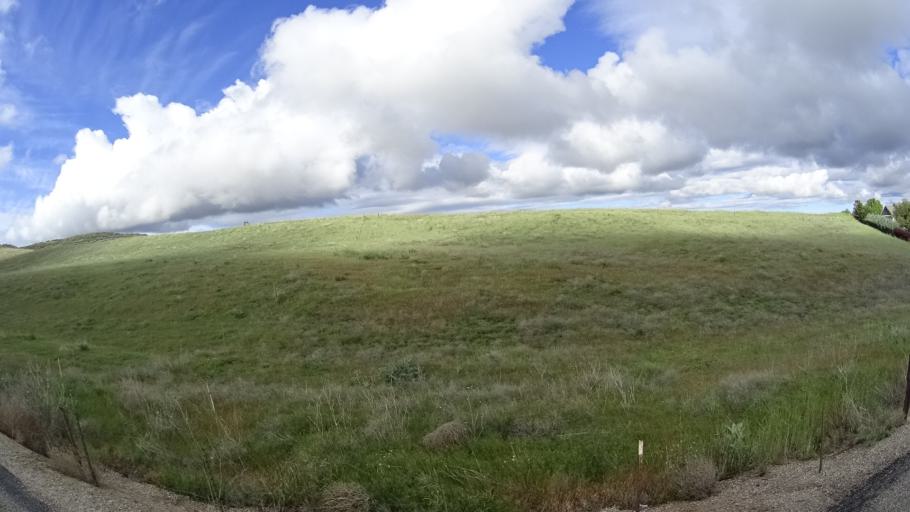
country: US
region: Idaho
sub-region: Ada County
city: Eagle
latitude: 43.7274
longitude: -116.2655
